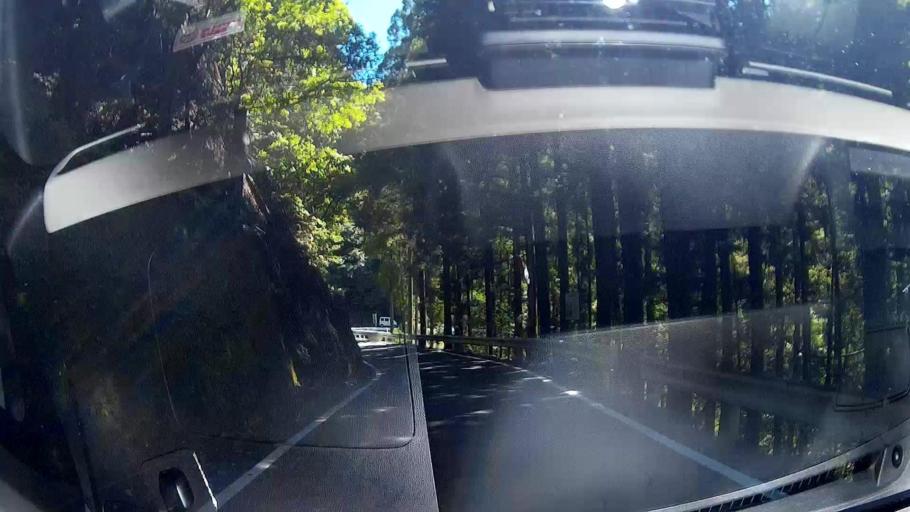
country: JP
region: Shizuoka
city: Shizuoka-shi
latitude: 35.1906
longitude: 138.2397
